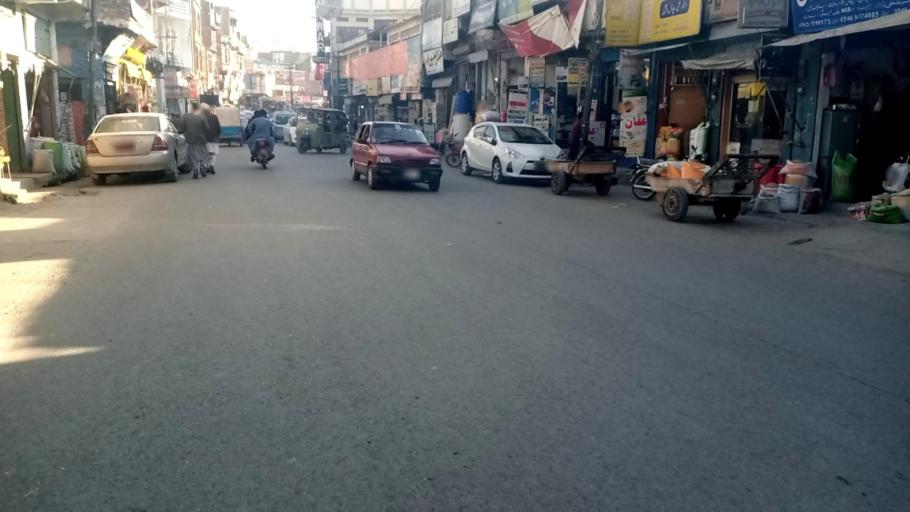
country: PK
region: Khyber Pakhtunkhwa
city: Mingora
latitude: 34.7777
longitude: 72.3573
